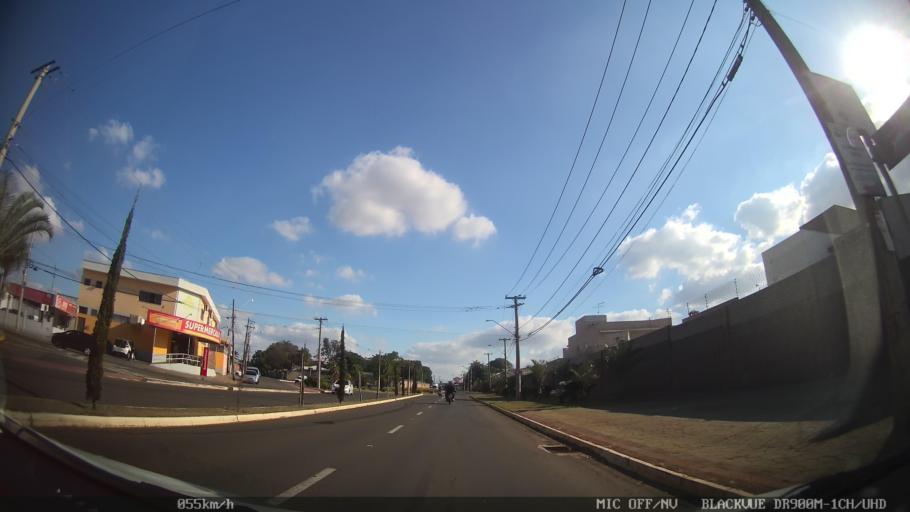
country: BR
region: Sao Paulo
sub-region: Nova Odessa
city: Nova Odessa
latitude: -22.7934
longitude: -47.3127
